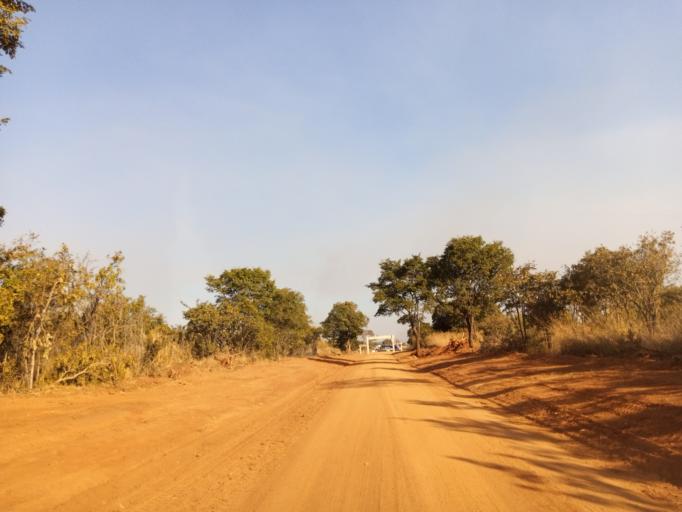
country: CD
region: Katanga
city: Lubumbashi
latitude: -11.3080
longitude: 27.2842
